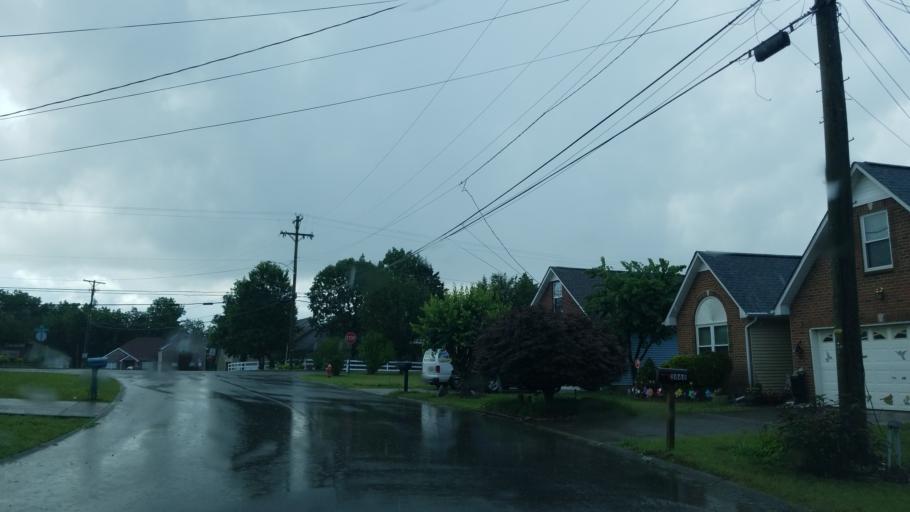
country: US
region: Tennessee
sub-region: Rutherford County
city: La Vergne
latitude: 36.0349
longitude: -86.5874
